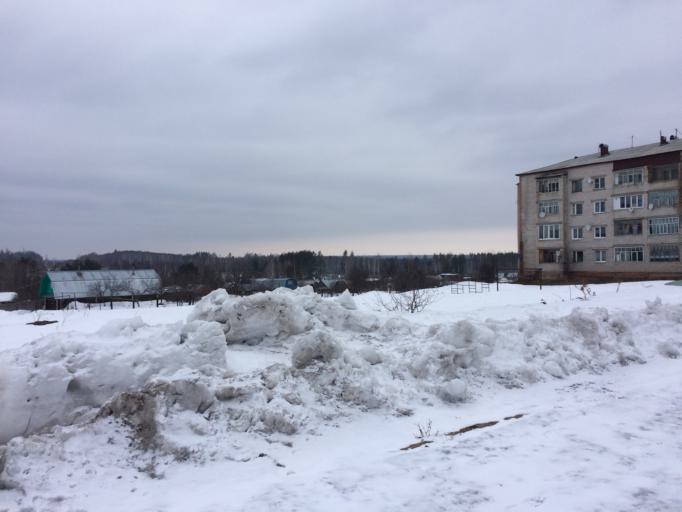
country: RU
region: Mariy-El
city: Mochalishche
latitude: 56.5440
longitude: 48.4016
